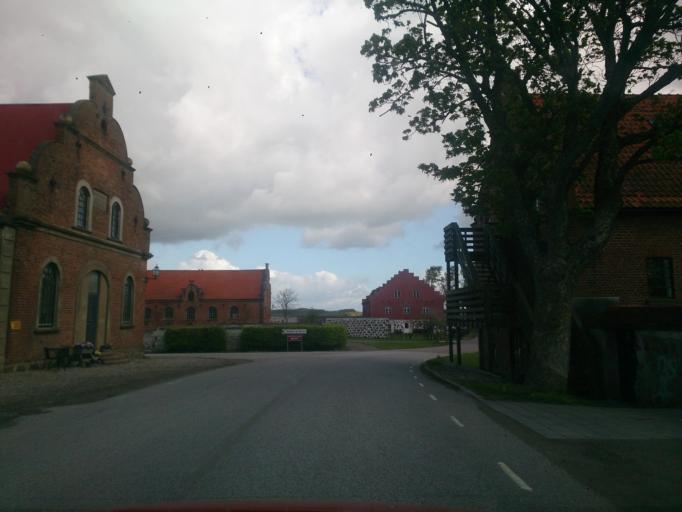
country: SE
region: Skane
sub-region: Ystads Kommun
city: Ystad
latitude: 55.4630
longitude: 13.7055
